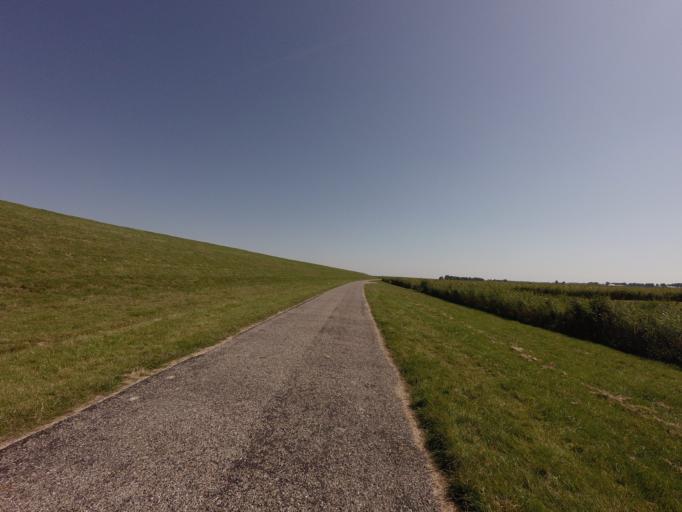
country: NL
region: Friesland
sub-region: Gemeente Dongeradeel
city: Anjum
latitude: 53.4015
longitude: 6.0919
